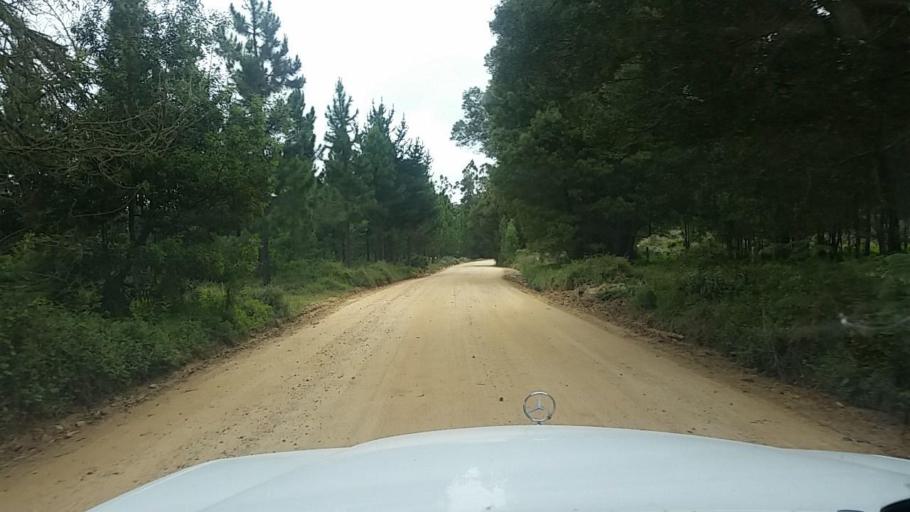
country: ZA
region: Western Cape
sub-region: Eden District Municipality
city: Knysna
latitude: -33.9888
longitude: 23.1467
